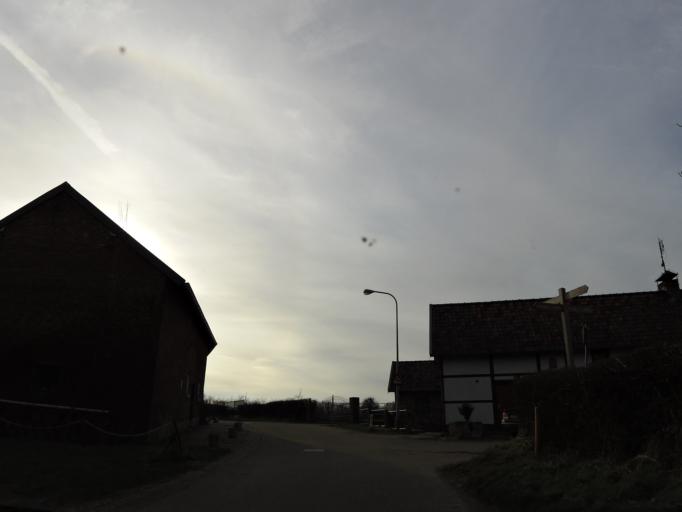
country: NL
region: Limburg
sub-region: Valkenburg aan de Geul
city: Schin op Geul
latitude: 50.7941
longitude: 5.8800
